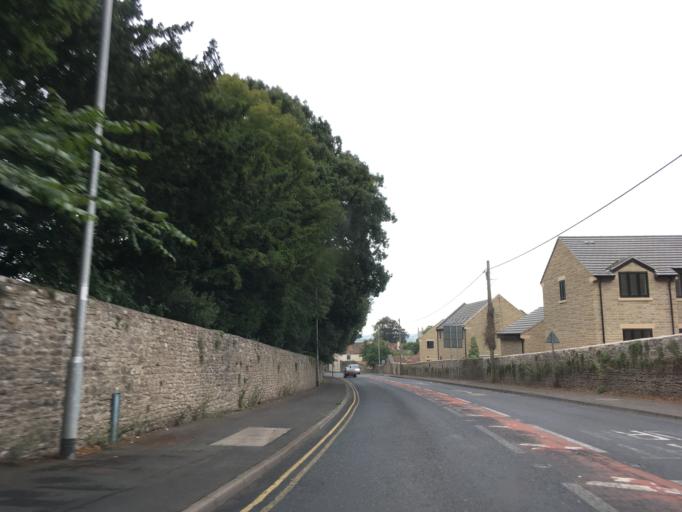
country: GB
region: England
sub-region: Somerset
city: Wells
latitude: 51.2154
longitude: -2.6458
